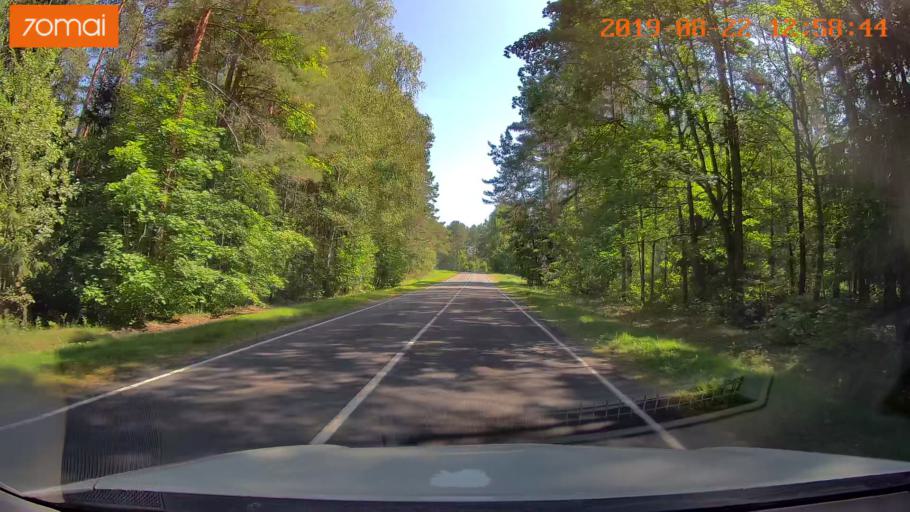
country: BY
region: Minsk
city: Prawdzinski
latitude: 53.4225
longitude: 27.7773
